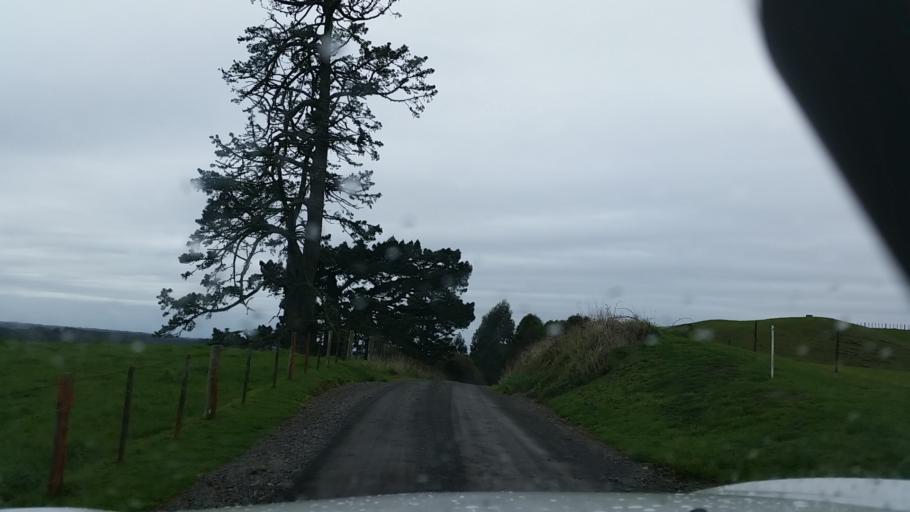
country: NZ
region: Bay of Plenty
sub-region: Rotorua District
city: Rotorua
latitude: -38.0241
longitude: 176.2841
